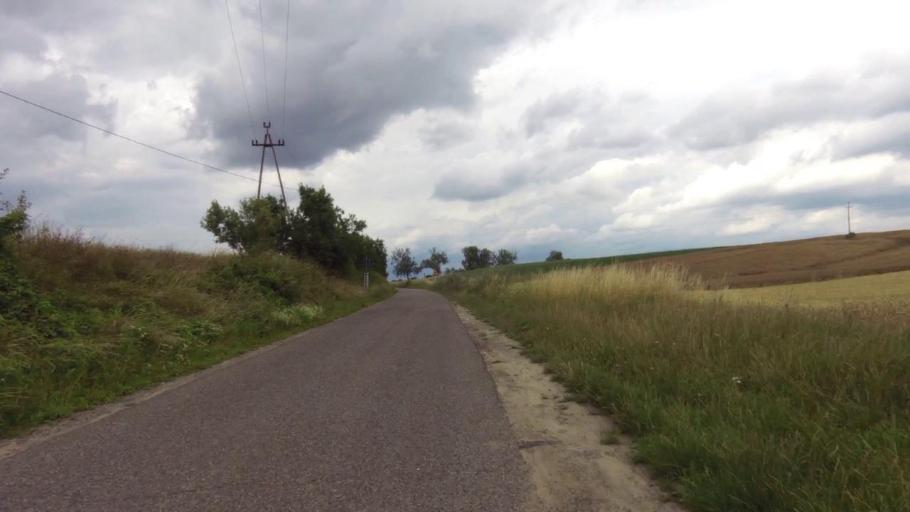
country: PL
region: West Pomeranian Voivodeship
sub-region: Powiat gryfinski
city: Moryn
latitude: 52.8740
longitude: 14.3910
